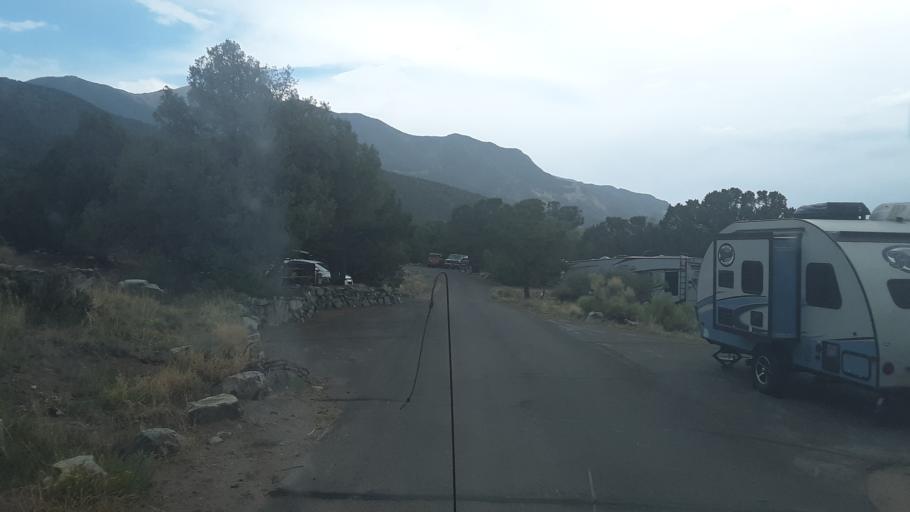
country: US
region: Colorado
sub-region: Custer County
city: Westcliffe
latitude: 37.7462
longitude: -105.5048
